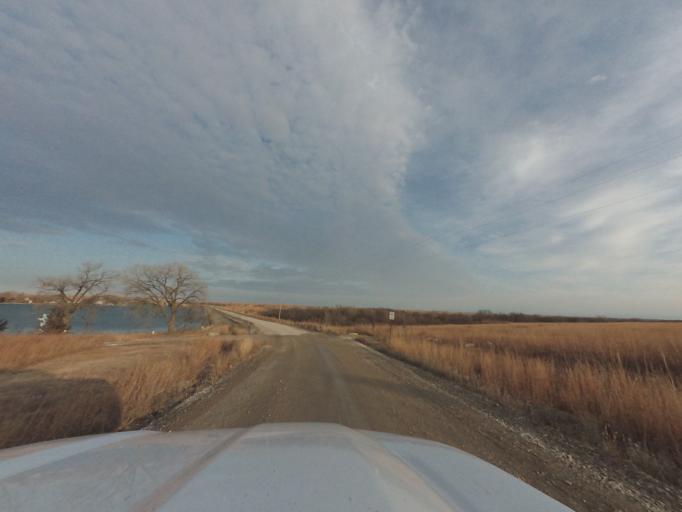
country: US
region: Kansas
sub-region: Morris County
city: Council Grove
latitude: 38.5228
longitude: -96.4113
